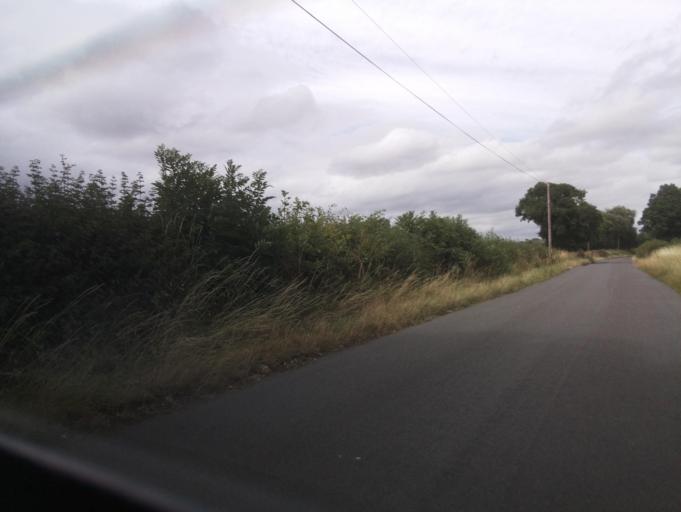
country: GB
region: England
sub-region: Warwickshire
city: Henley in Arden
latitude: 52.2678
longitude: -1.7678
